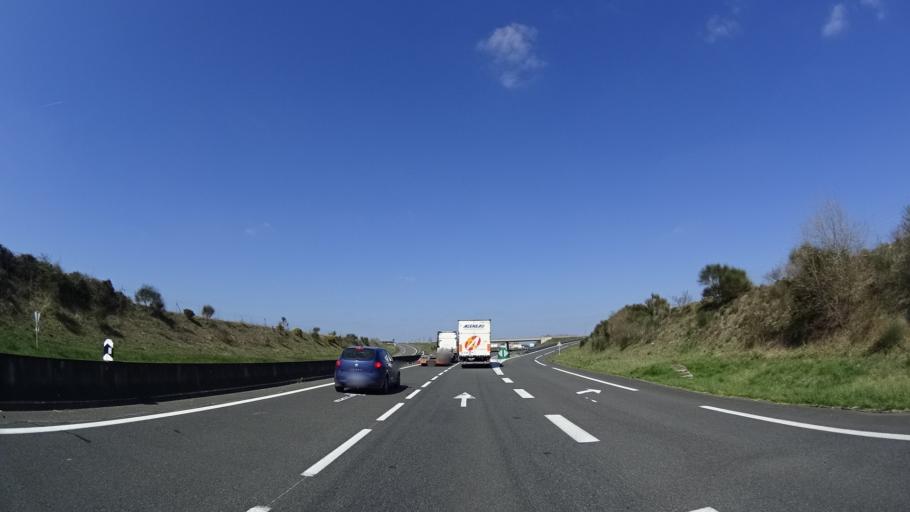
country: FR
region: Pays de la Loire
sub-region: Departement de Maine-et-Loire
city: Saint-Jean
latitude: 47.2535
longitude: -0.3316
